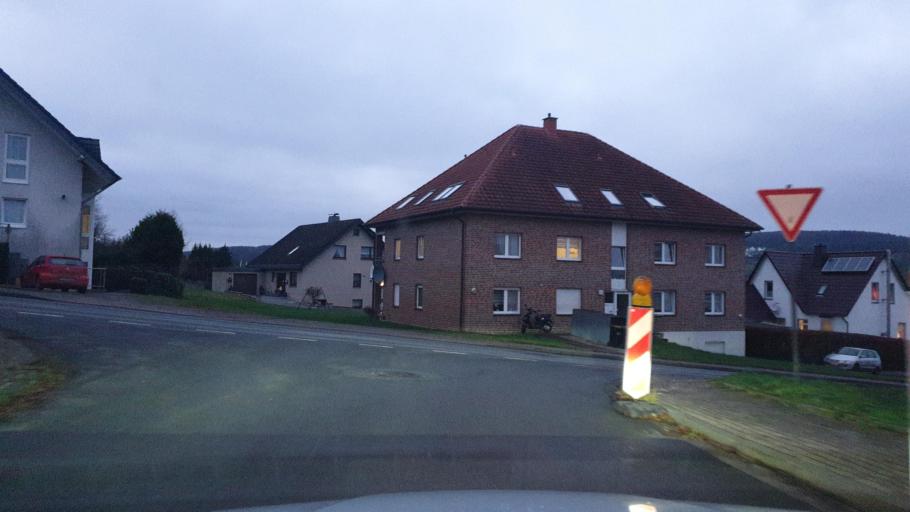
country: DE
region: North Rhine-Westphalia
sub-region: Regierungsbezirk Detmold
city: Vlotho
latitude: 52.1632
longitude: 8.8670
